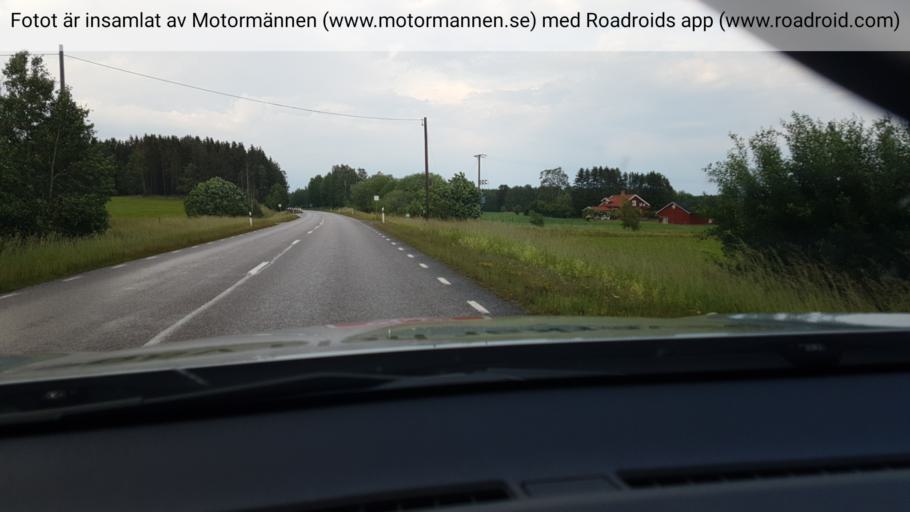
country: SE
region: Vaestra Goetaland
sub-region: Hjo Kommun
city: Hjo
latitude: 58.2403
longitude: 14.2272
